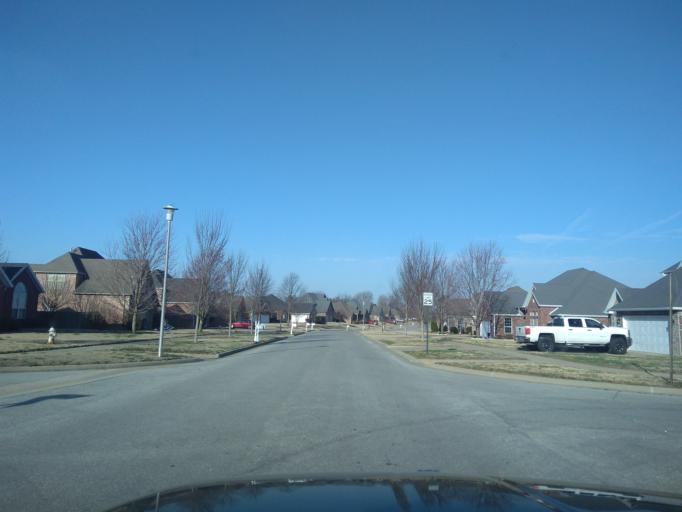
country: US
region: Arkansas
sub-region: Washington County
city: Farmington
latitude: 36.0711
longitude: -94.2493
